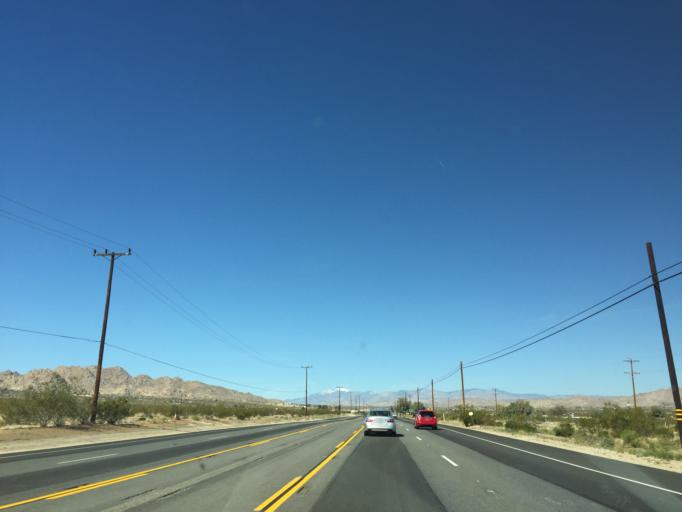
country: US
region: California
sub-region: San Bernardino County
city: Joshua Tree
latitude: 34.1352
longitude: -116.2428
